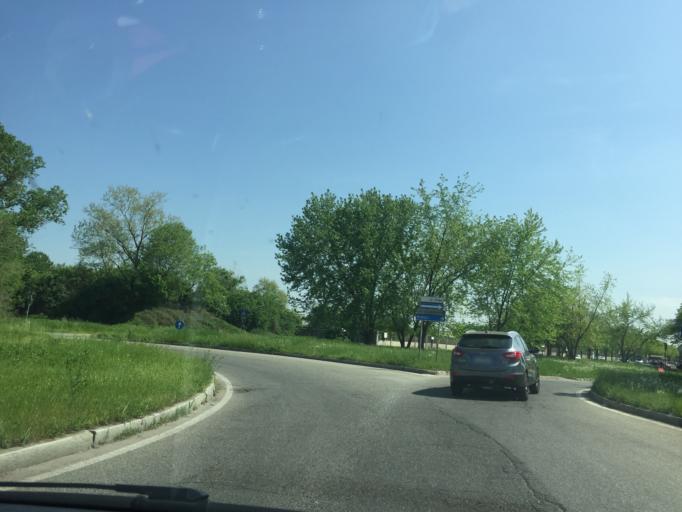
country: IT
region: Piedmont
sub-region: Provincia di Torino
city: Lesna
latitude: 45.0592
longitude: 7.6146
